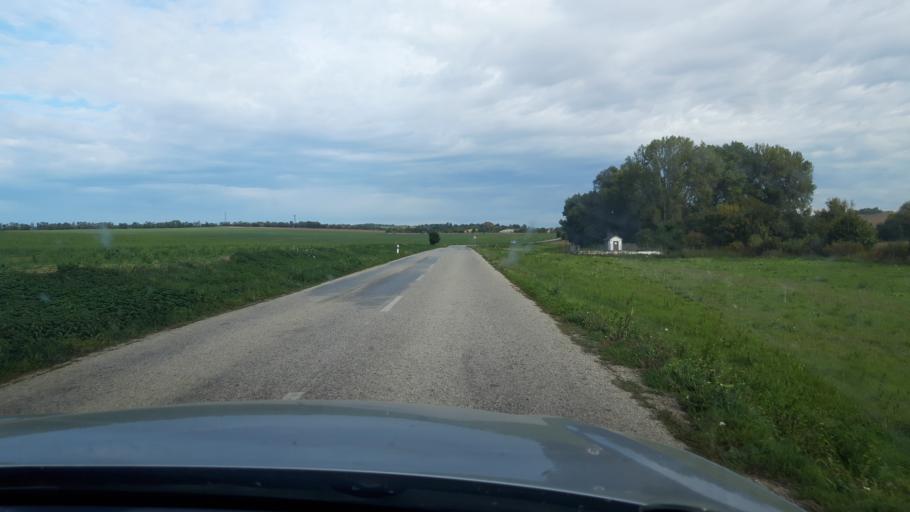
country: SK
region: Nitriansky
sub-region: Okres Nitra
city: Vrable
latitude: 48.1192
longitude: 18.3340
